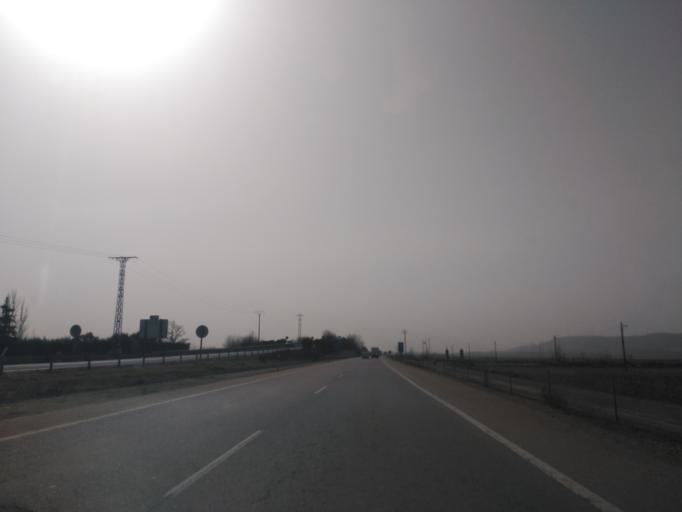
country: ES
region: Castille and Leon
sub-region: Provincia de Palencia
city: Venta de Banos
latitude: 41.9262
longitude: -4.5048
